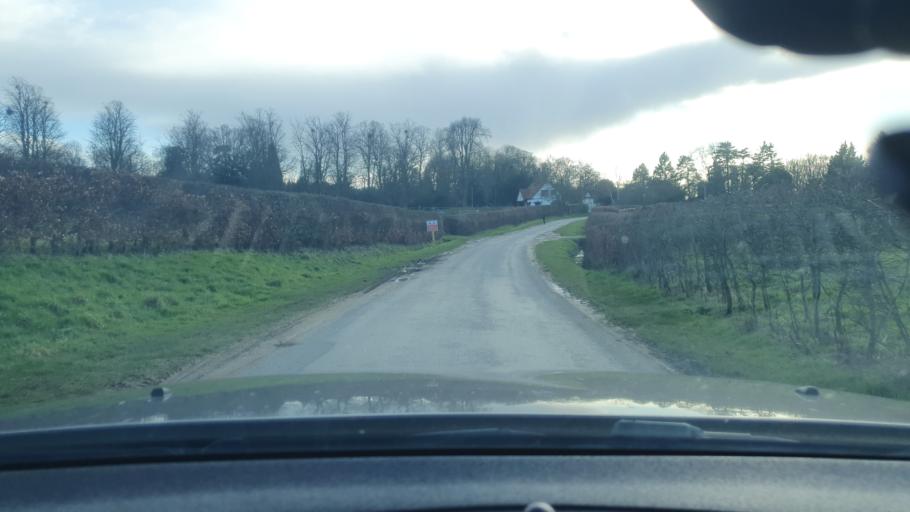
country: GB
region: England
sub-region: Wokingham
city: Wargrave
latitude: 51.5217
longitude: -0.8429
